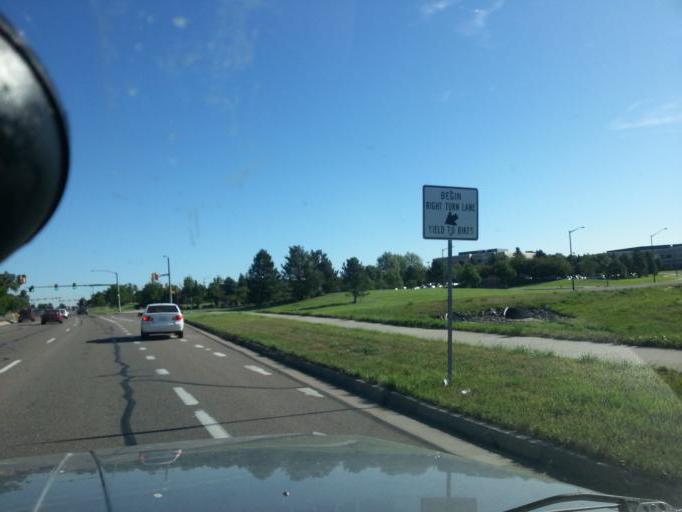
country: US
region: Colorado
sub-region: Larimer County
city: Fort Collins
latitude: 40.5198
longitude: -105.0392
